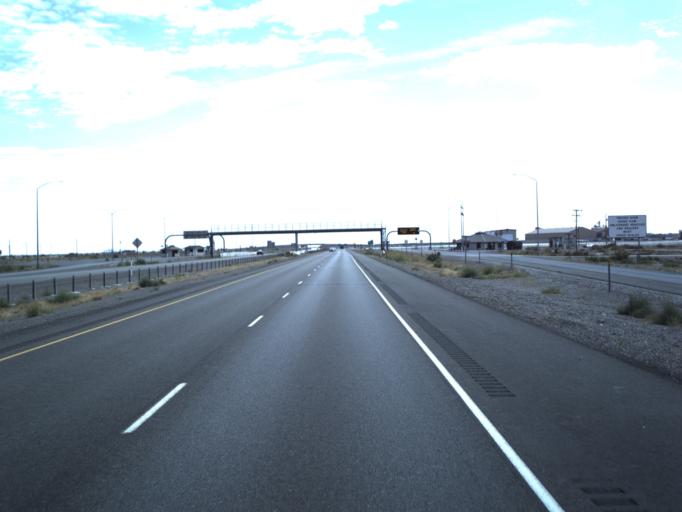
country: US
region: Utah
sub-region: Tooele County
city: Wendover
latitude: 40.7456
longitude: -113.9935
